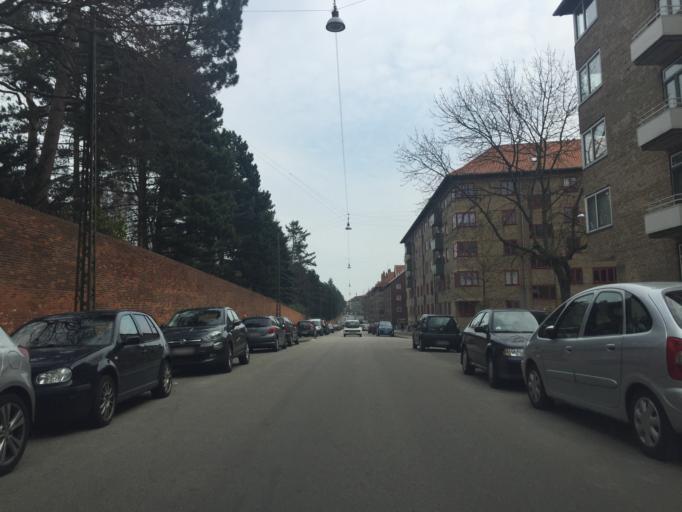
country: DK
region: Capital Region
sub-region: Frederiksberg Kommune
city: Frederiksberg
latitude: 55.7114
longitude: 12.5227
